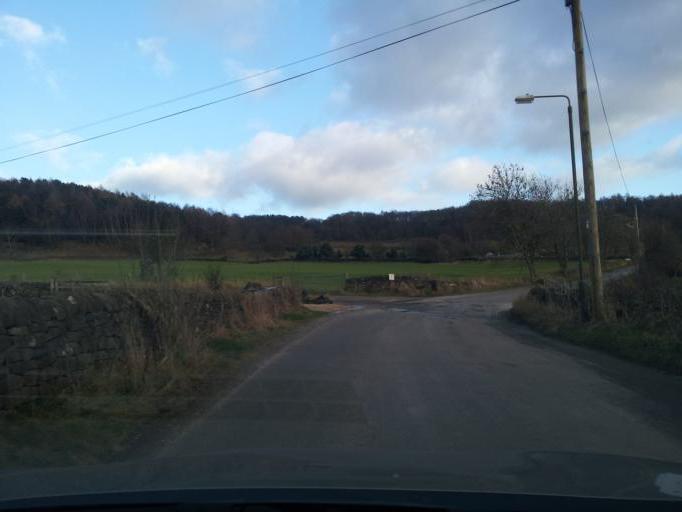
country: GB
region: England
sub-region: Derbyshire
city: Bakewell
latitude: 53.1599
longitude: -1.6527
